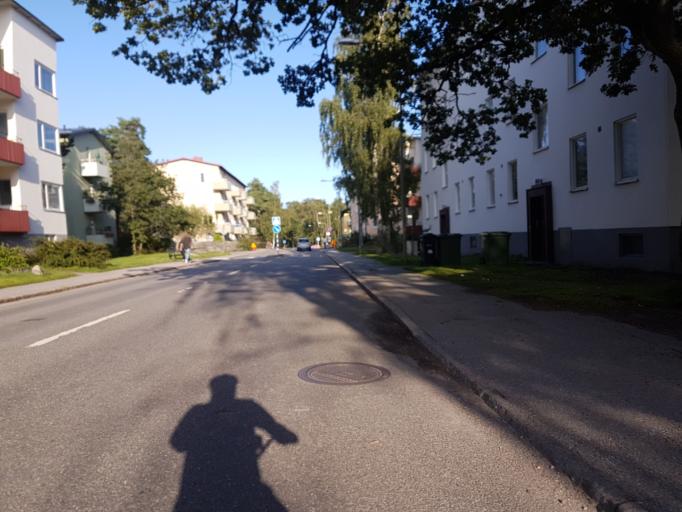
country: SE
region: Stockholm
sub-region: Stockholms Kommun
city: OEstermalm
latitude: 59.2954
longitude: 18.1039
